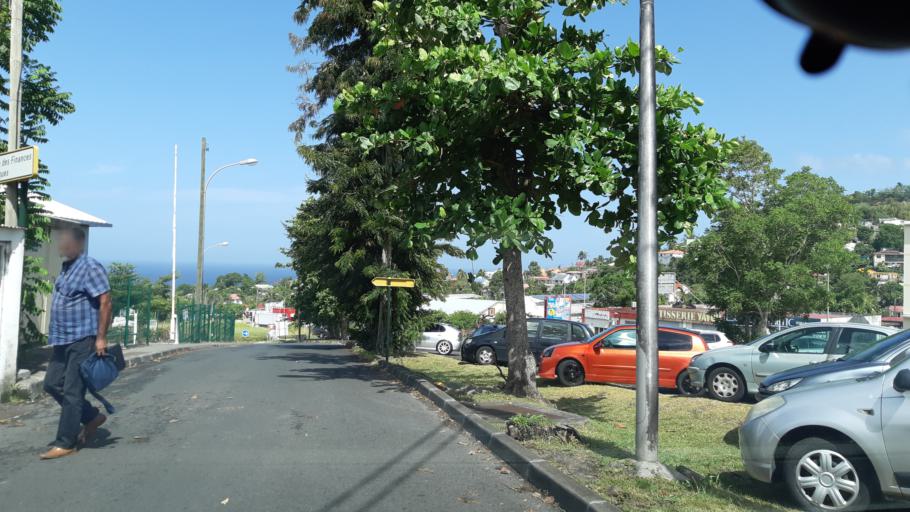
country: GP
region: Guadeloupe
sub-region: Guadeloupe
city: Basse-Terre
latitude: 16.0016
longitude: -61.7171
